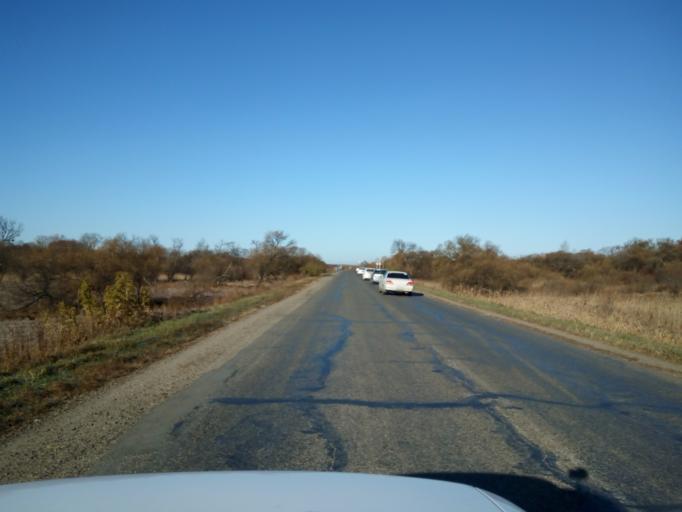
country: RU
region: Primorskiy
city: Dal'nerechensk
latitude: 45.9173
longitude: 133.7798
